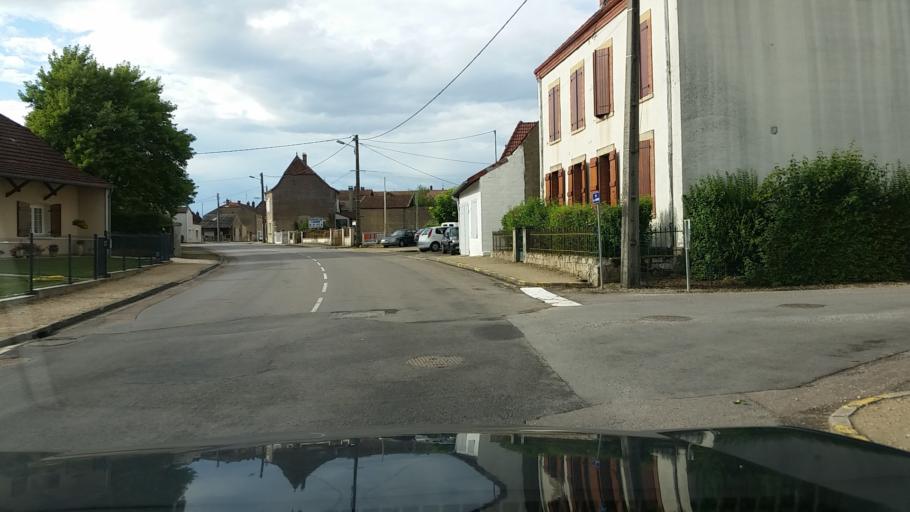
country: FR
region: Bourgogne
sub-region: Departement de Saone-et-Loire
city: Saint-Germain-du-Bois
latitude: 46.7500
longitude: 5.2444
